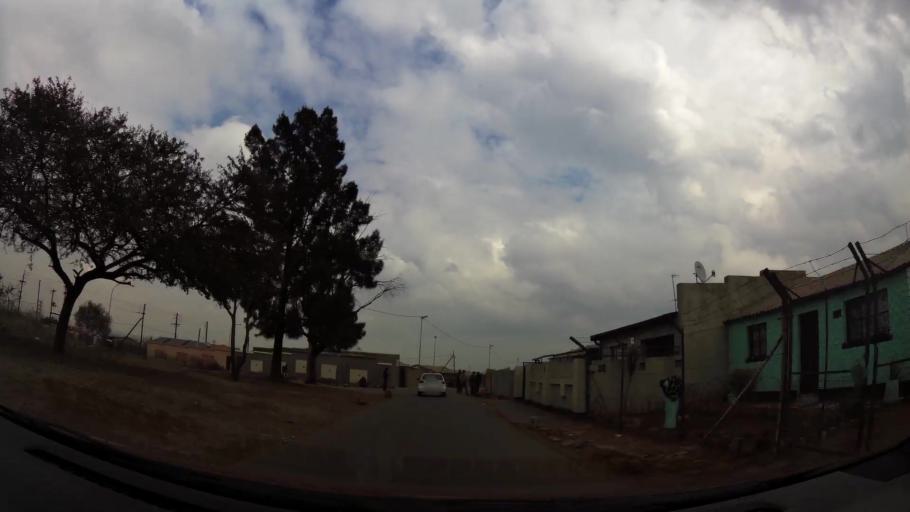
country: ZA
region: Gauteng
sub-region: City of Johannesburg Metropolitan Municipality
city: Soweto
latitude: -26.2579
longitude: 27.8260
